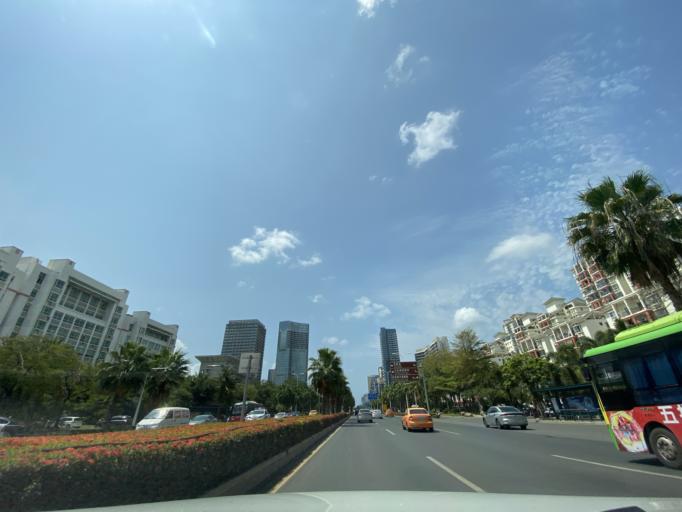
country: CN
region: Hainan
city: Sanya
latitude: 18.2797
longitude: 109.5119
